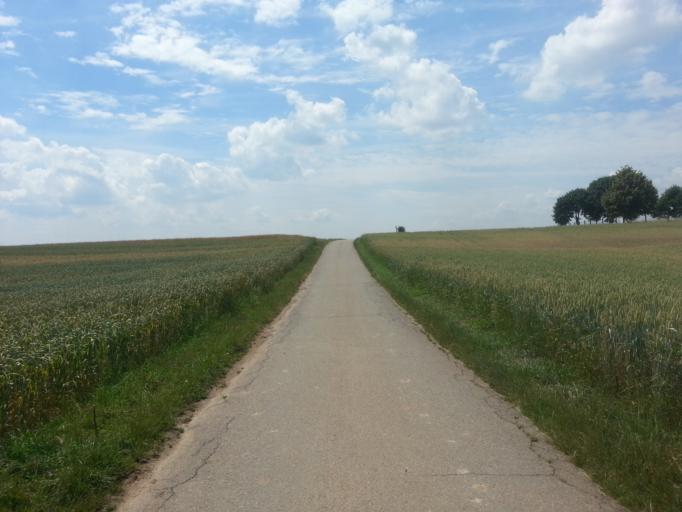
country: DE
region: Baden-Wuerttemberg
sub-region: Karlsruhe Region
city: Edingen-Neckarhausen
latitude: 49.4360
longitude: 8.6227
